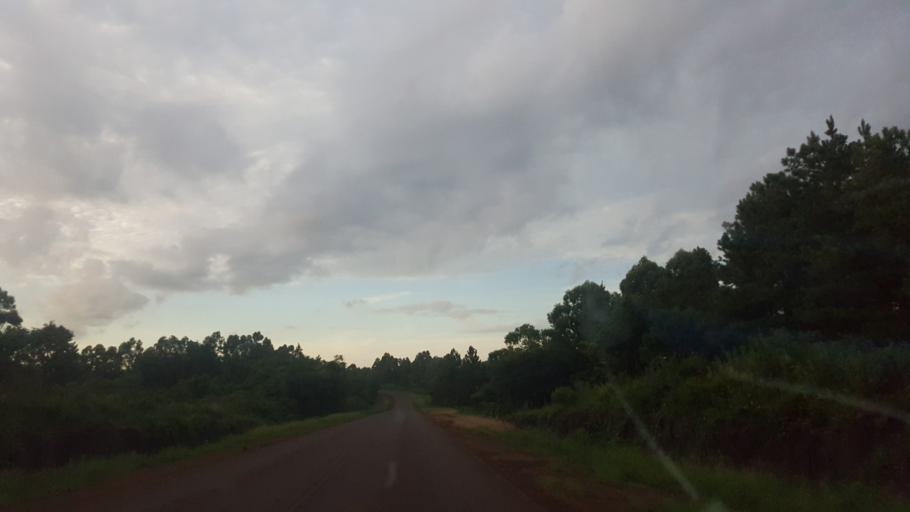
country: AR
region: Misiones
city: Dos de Mayo
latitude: -26.9466
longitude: -54.7145
